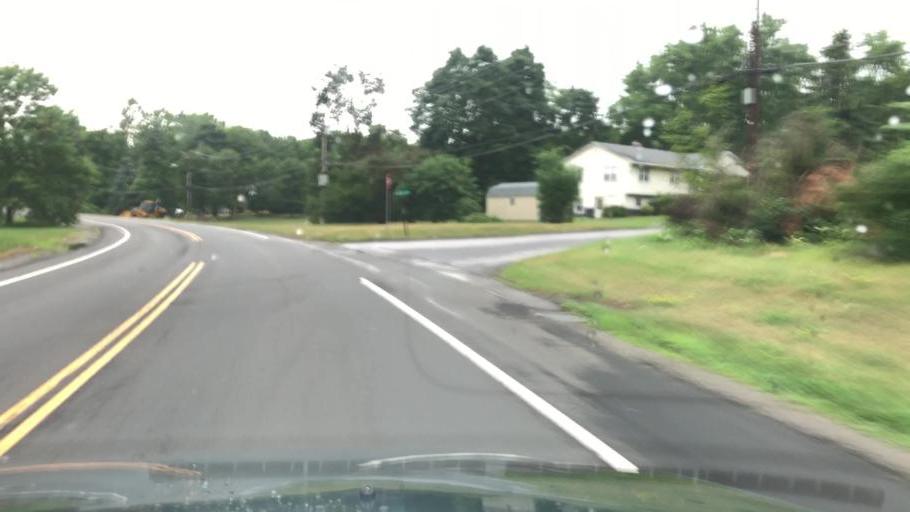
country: US
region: New York
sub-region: Dutchess County
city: Beacon
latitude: 41.5242
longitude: -73.9405
